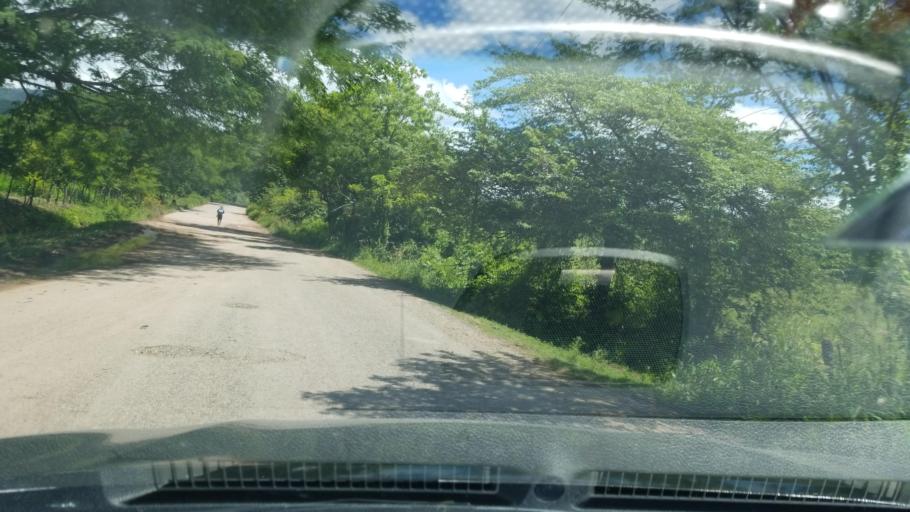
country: HN
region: Francisco Morazan
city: San Juan de Flores
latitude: 14.3117
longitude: -87.0365
